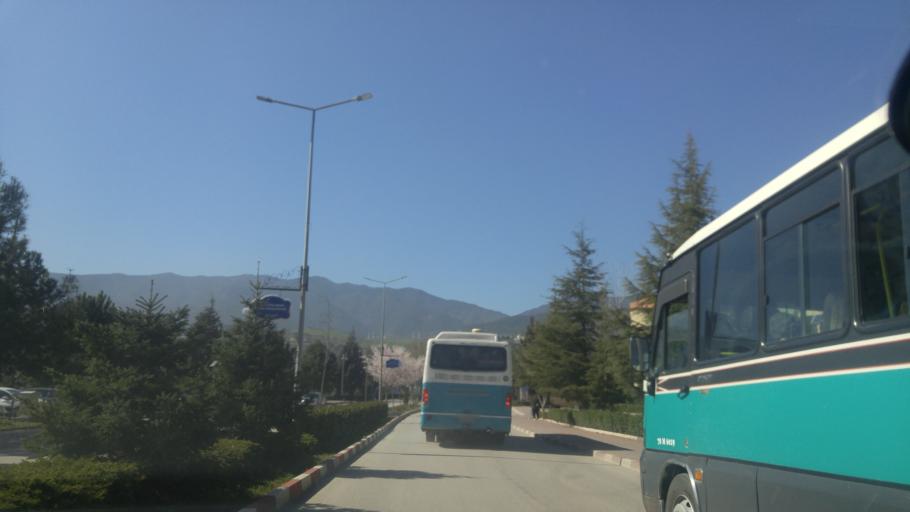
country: TR
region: Karabuk
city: Karabuk
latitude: 41.2123
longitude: 32.6535
